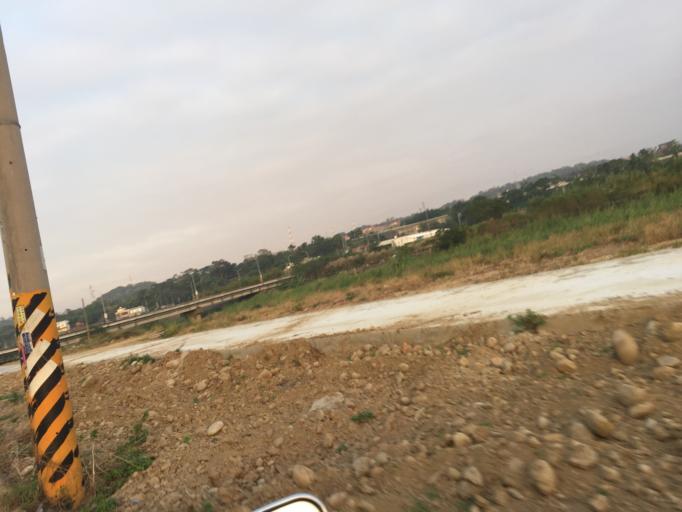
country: TW
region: Taiwan
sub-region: Miaoli
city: Miaoli
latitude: 24.4934
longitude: 120.7789
